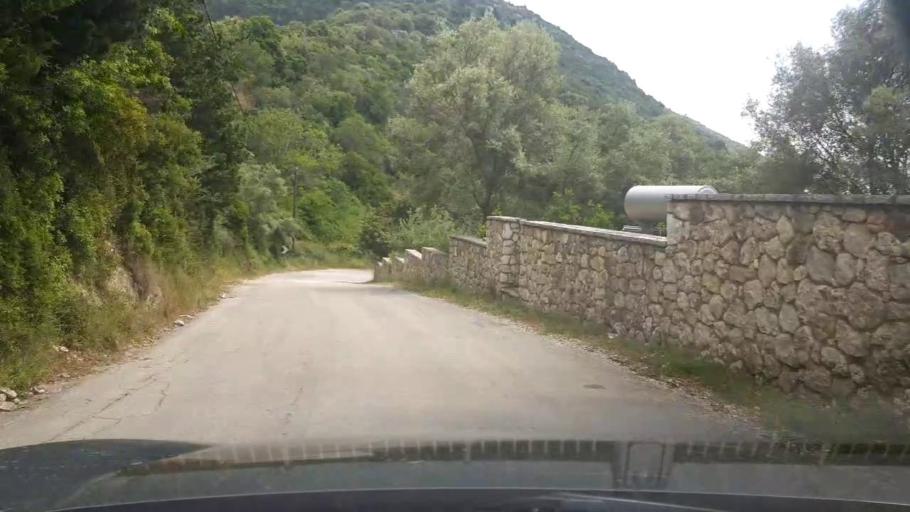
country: GR
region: Ionian Islands
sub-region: Lefkada
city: Nidri
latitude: 38.6446
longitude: 20.7007
